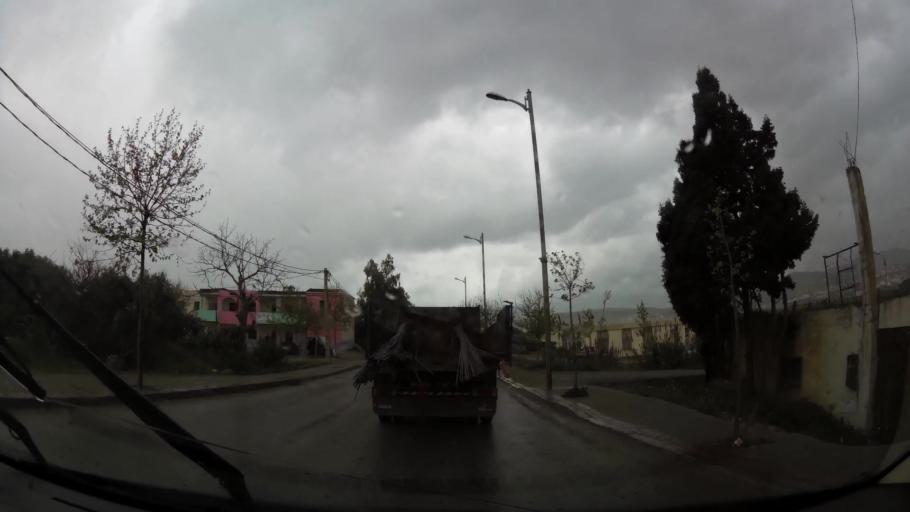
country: MA
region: Tanger-Tetouan
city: Tetouan
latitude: 35.5580
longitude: -5.4094
